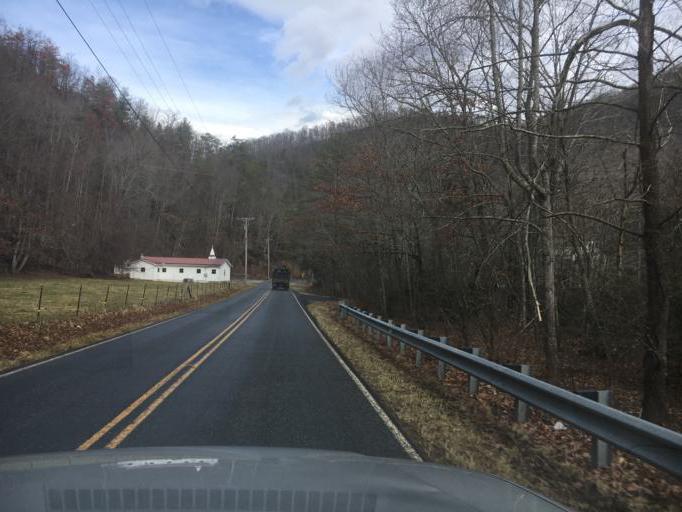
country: US
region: North Carolina
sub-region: Haywood County
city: Canton
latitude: 35.4099
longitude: -82.8113
